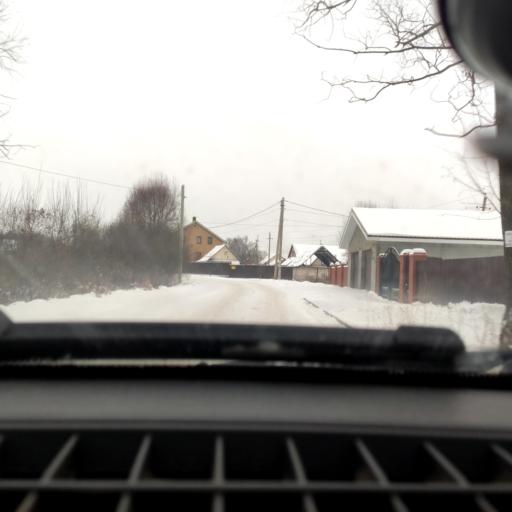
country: RU
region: Bashkortostan
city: Mikhaylovka
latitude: 54.7743
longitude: 55.8221
